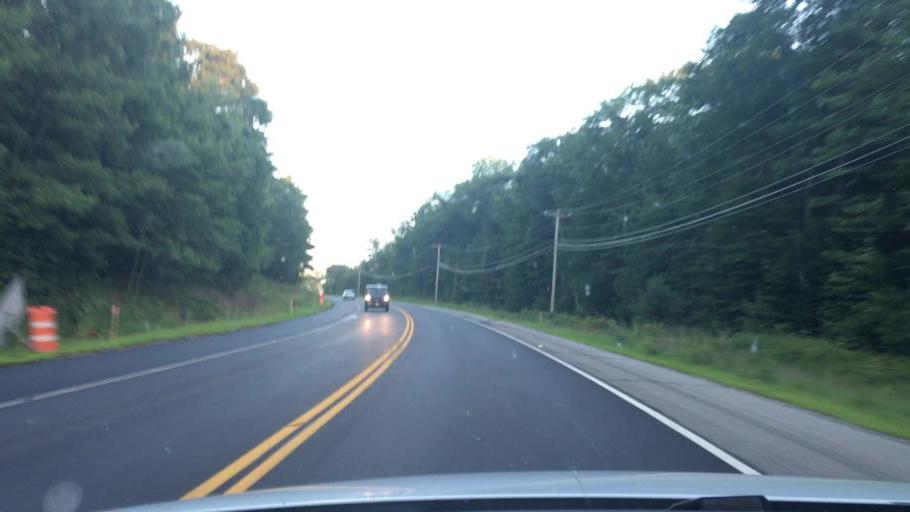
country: US
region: Maine
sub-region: Androscoggin County
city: Turner
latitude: 44.2654
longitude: -70.2660
